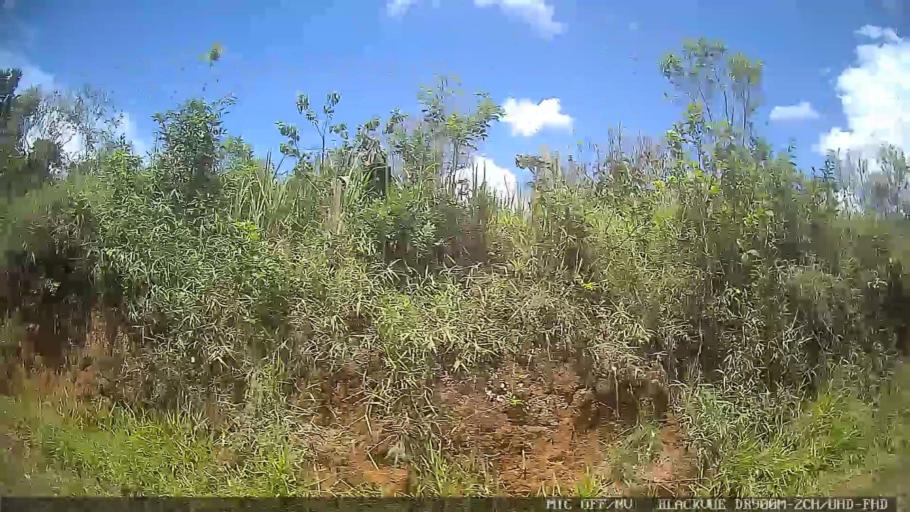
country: BR
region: Minas Gerais
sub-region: Extrema
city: Extrema
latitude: -22.7544
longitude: -46.4359
